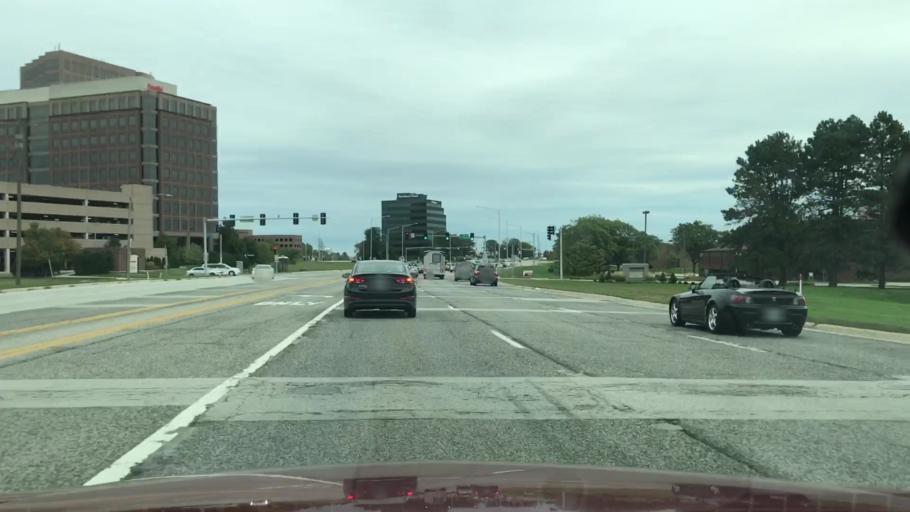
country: US
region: Illinois
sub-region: DuPage County
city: Oakbrook Terrace
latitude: 41.8446
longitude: -87.9869
